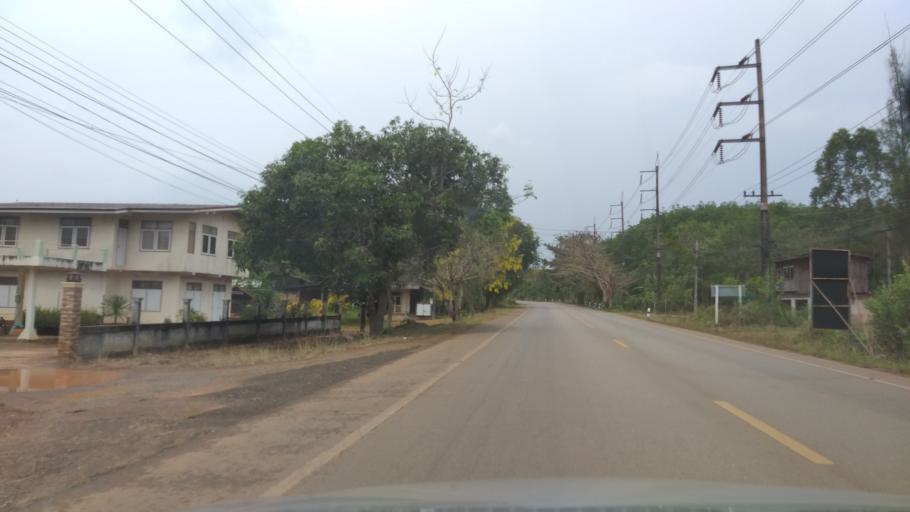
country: TH
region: Trat
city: Laem Ngop
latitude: 12.2479
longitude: 102.2933
